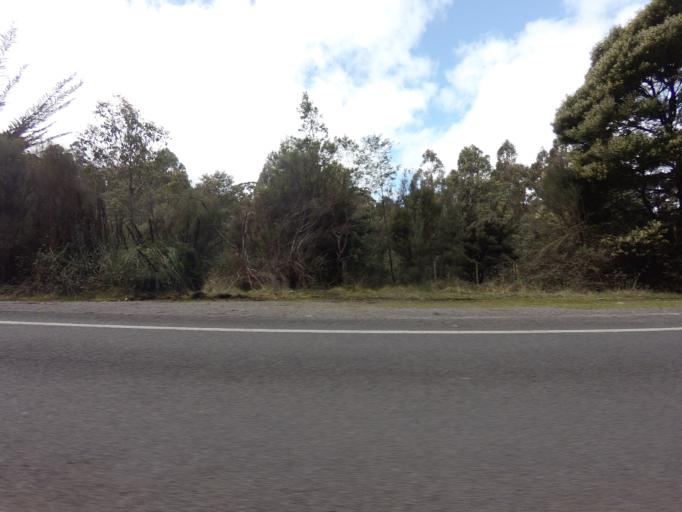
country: AU
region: Tasmania
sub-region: Huon Valley
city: Geeveston
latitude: -43.4085
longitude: 146.9588
